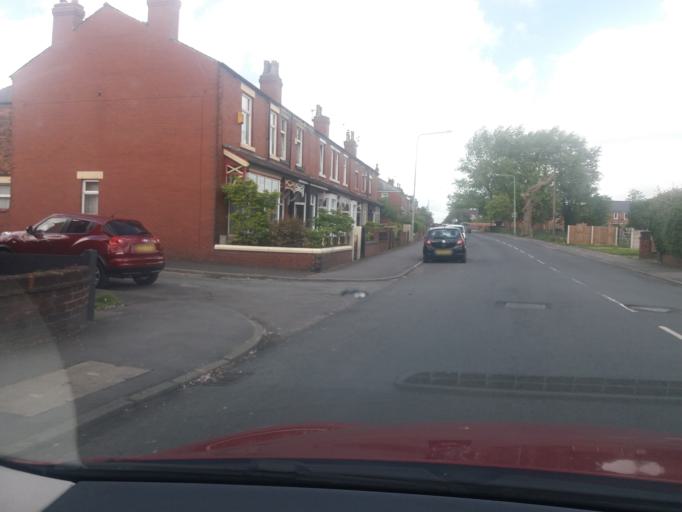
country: GB
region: England
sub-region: Lancashire
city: Chorley
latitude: 53.6418
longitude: -2.6344
